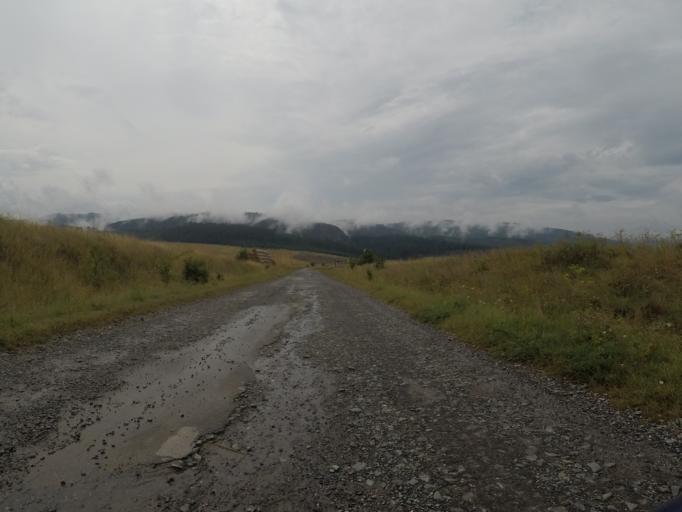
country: SK
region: Kosicky
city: Spisska Nova Ves
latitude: 48.9687
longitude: 20.4545
